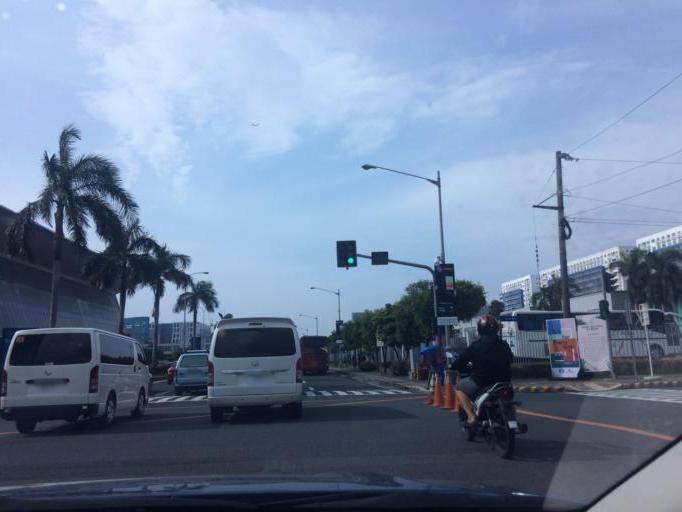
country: PH
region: Metro Manila
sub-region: Makati City
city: Makati City
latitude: 14.5312
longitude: 120.9847
